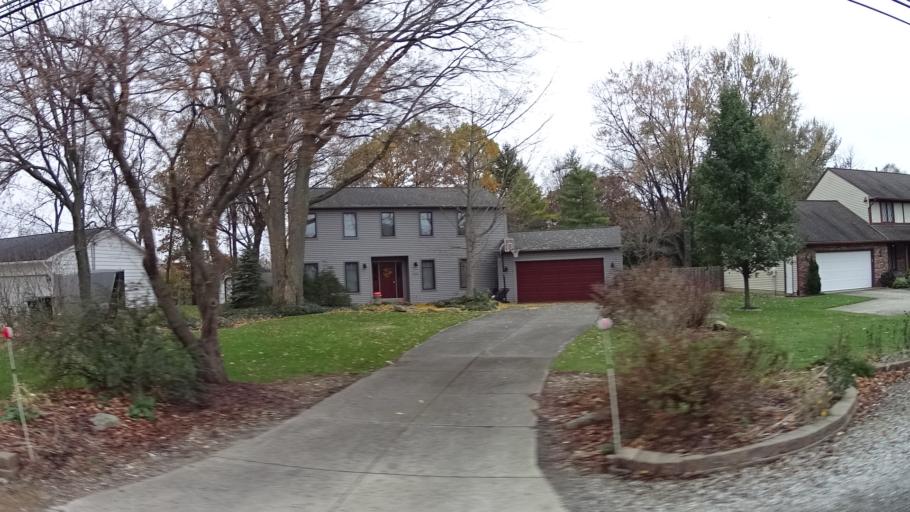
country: US
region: Ohio
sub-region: Lorain County
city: Sheffield
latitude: 41.4138
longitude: -82.0905
